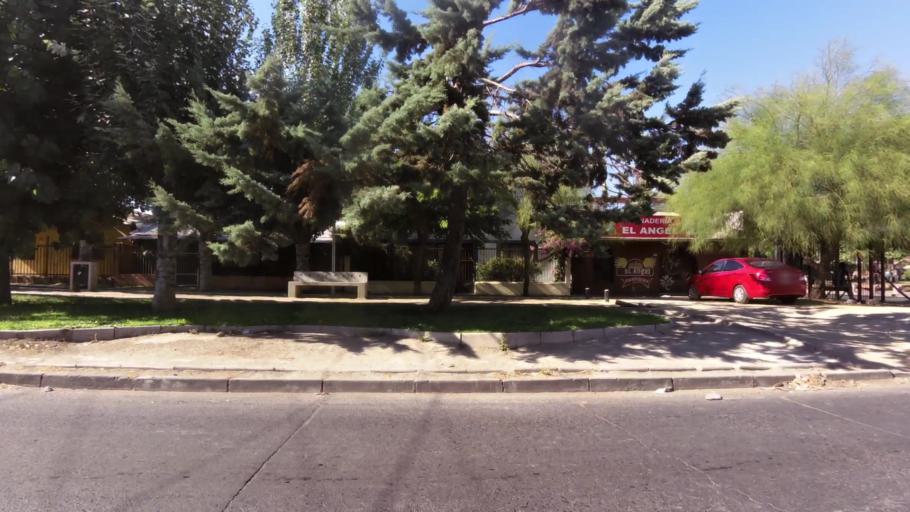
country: CL
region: Maule
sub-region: Provincia de Curico
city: Curico
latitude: -34.9944
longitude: -71.2479
